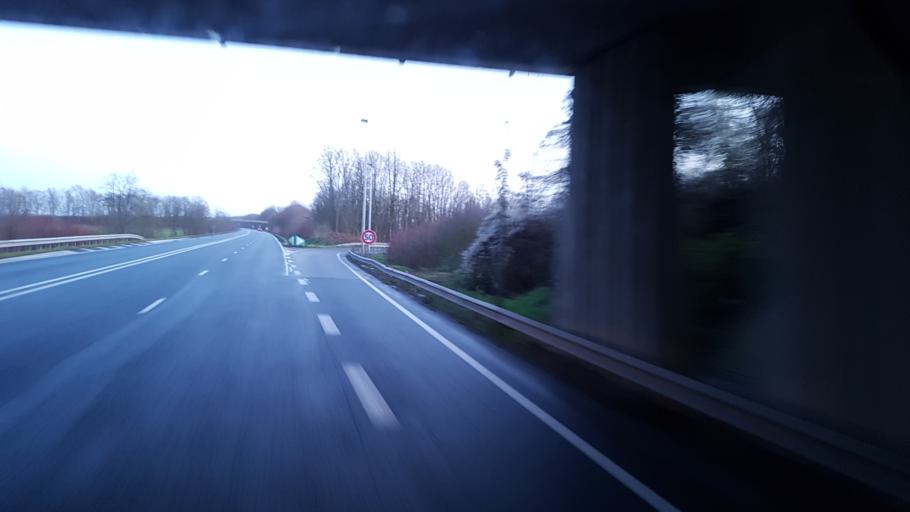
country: FR
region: Nord-Pas-de-Calais
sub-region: Departement du Nord
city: Ferin
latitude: 50.3354
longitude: 3.0898
